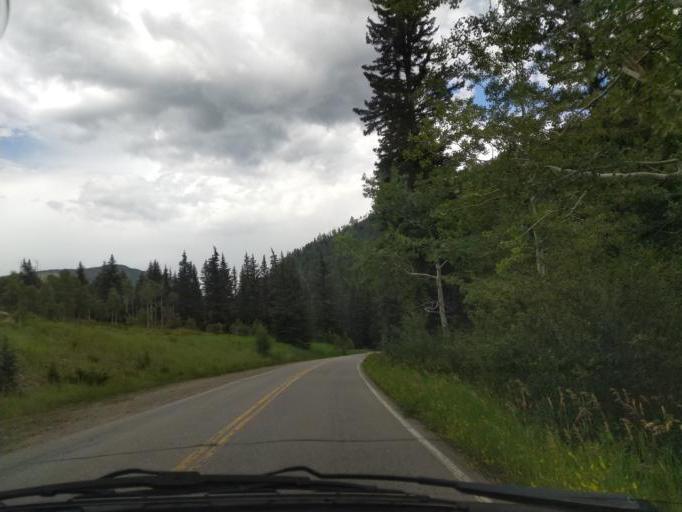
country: US
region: Colorado
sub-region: Garfield County
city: Carbondale
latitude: 39.1031
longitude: -107.2649
